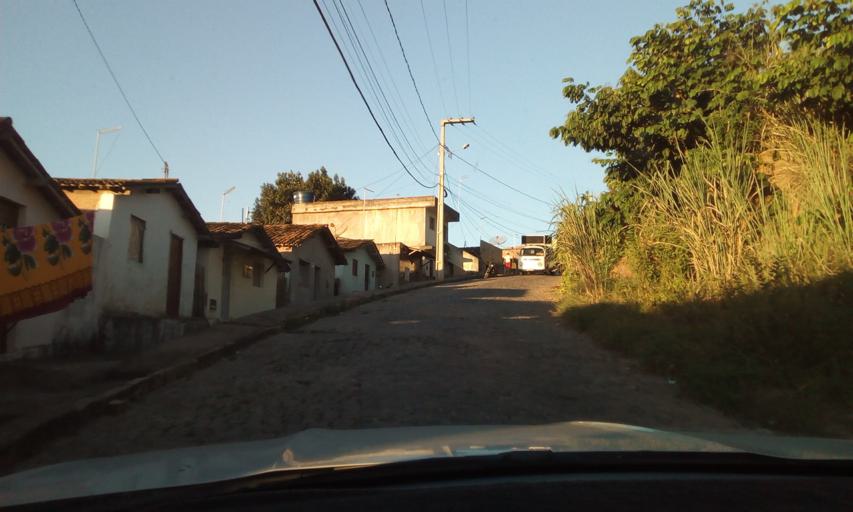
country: BR
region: Paraiba
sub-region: Areia
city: Areia
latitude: -6.9723
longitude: -35.7076
